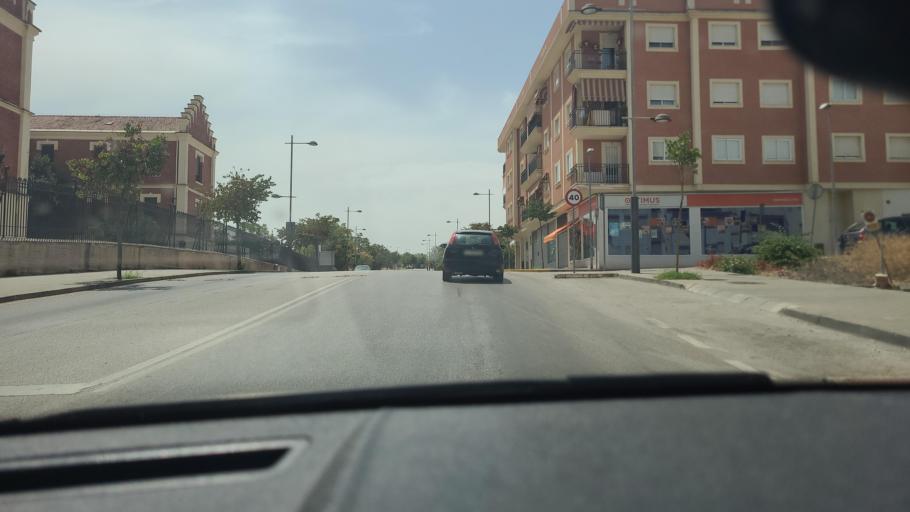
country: ES
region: Andalusia
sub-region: Provincia de Jaen
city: Linares
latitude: 38.0888
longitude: -3.6288
